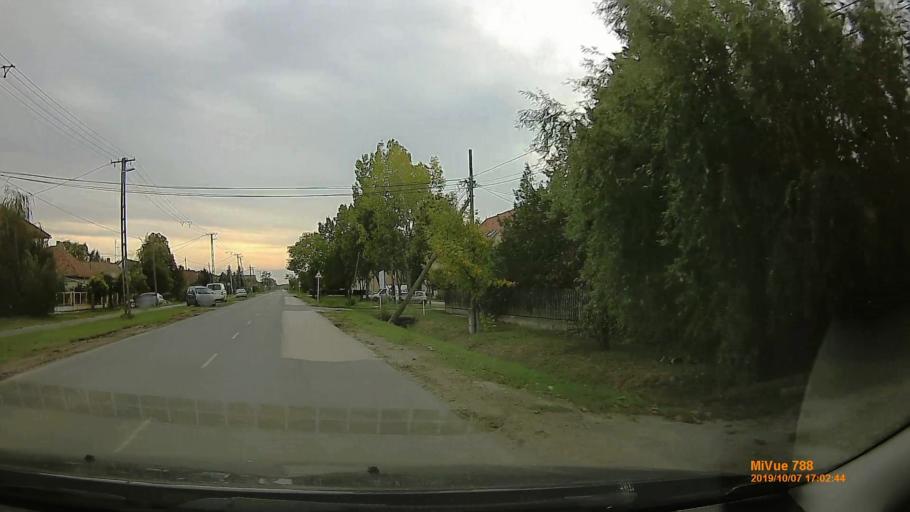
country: HU
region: Bekes
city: Szarvas
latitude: 46.8505
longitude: 20.5566
